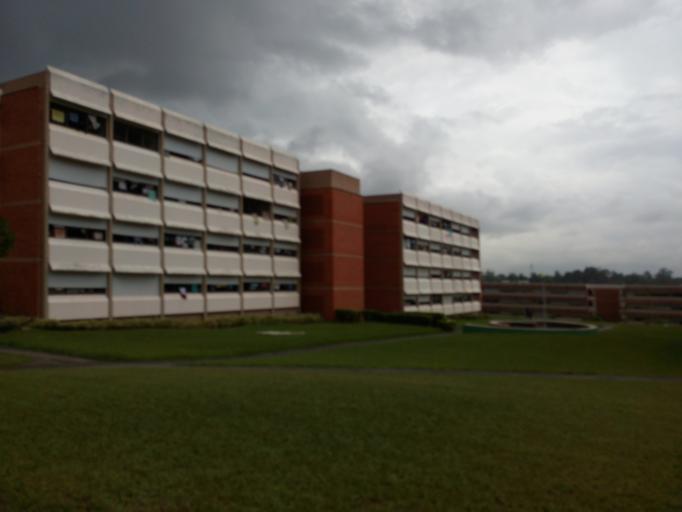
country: CI
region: Lagunes
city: Abidjan
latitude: 5.3400
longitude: -3.9888
